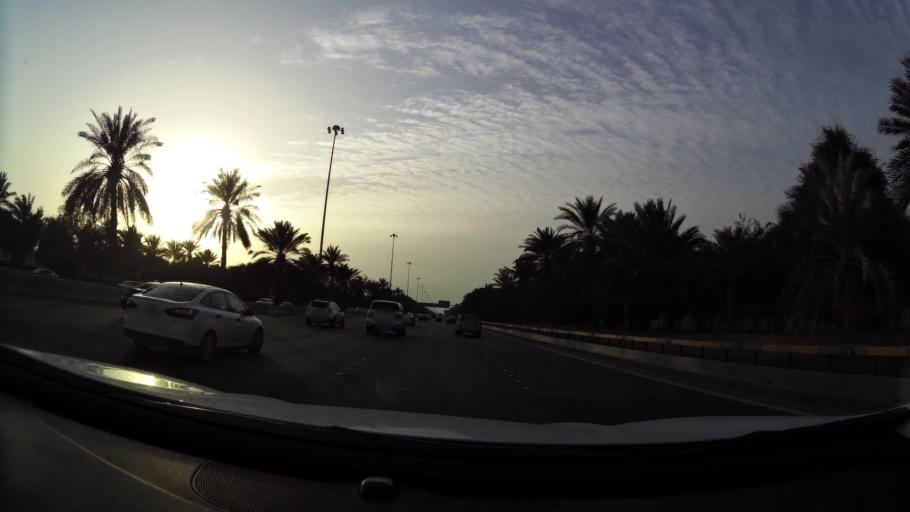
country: AE
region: Abu Dhabi
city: Abu Dhabi
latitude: 24.3959
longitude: 54.5141
